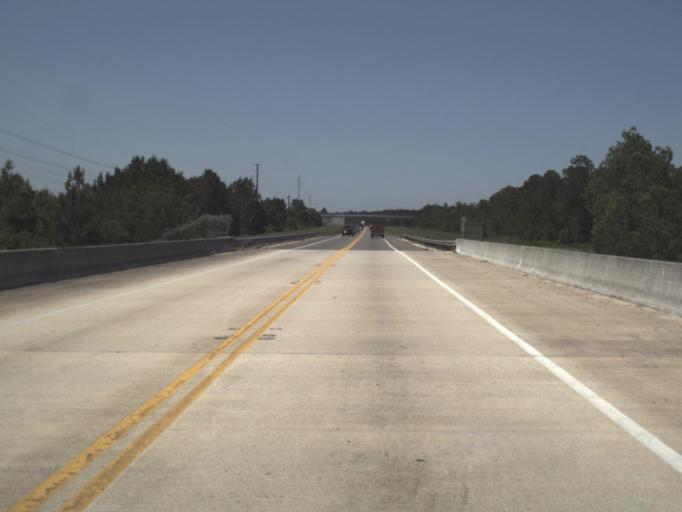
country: US
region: Florida
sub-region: Clay County
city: Lakeside
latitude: 30.1645
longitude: -81.8313
